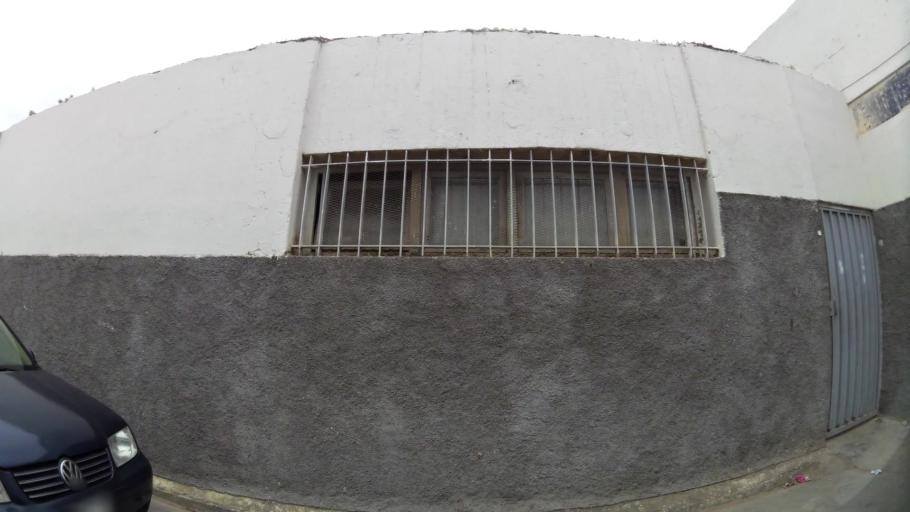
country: MA
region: Fes-Boulemane
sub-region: Fes
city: Fes
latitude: 34.0574
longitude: -4.9746
